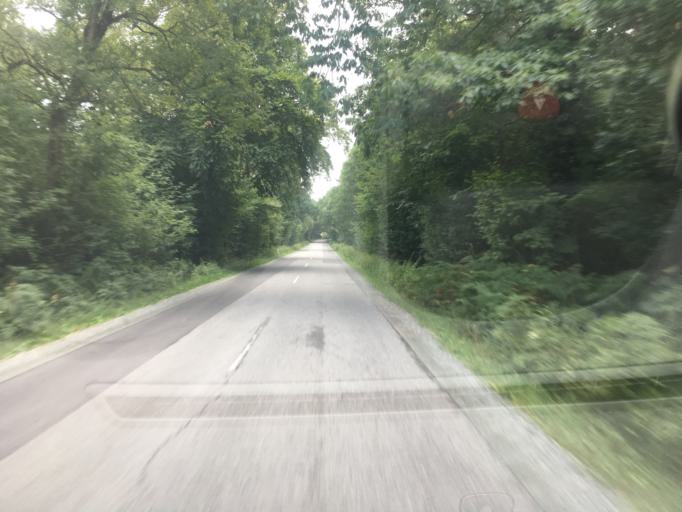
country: DK
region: South Denmark
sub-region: Tonder Kommune
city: Logumkloster
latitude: 55.0118
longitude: 8.9675
